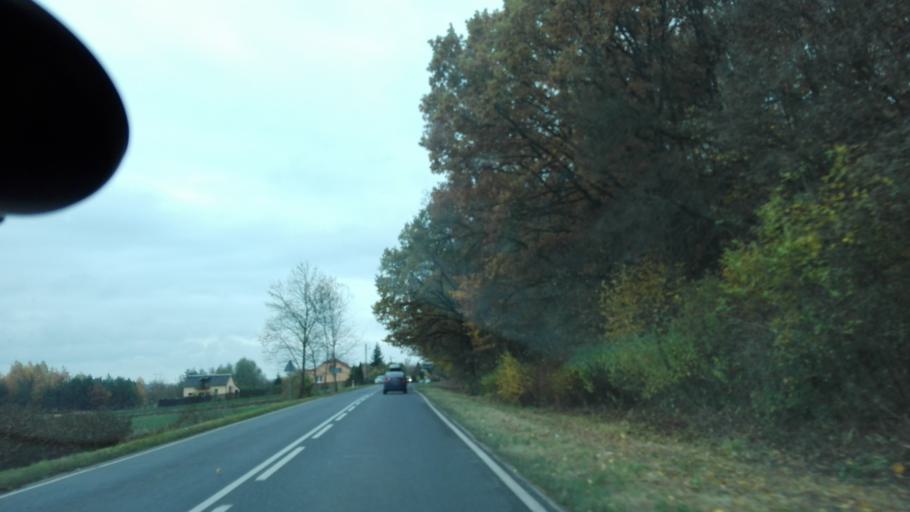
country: PL
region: Lublin Voivodeship
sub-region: Powiat pulawski
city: Pulawy
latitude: 51.4238
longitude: 21.9236
